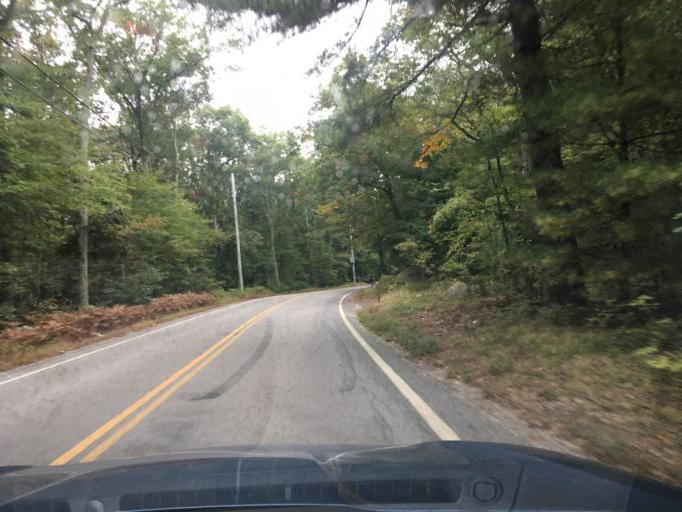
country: US
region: Rhode Island
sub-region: Washington County
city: Exeter
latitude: 41.6160
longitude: -71.5642
